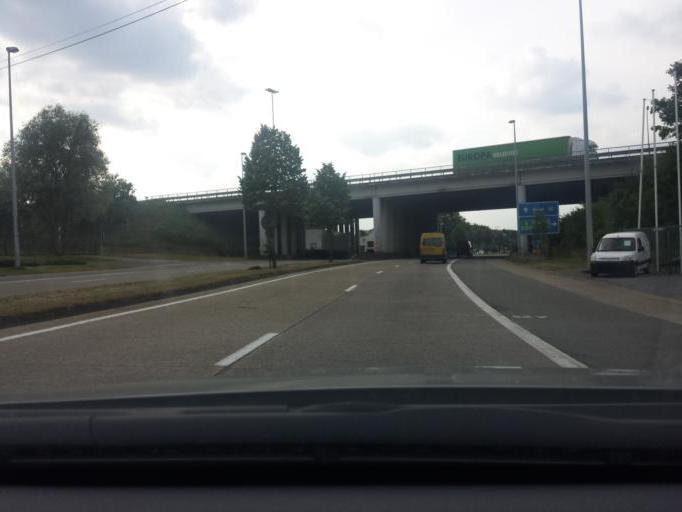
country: BE
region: Flanders
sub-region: Provincie Limburg
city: Halen
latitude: 50.9626
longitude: 5.0814
